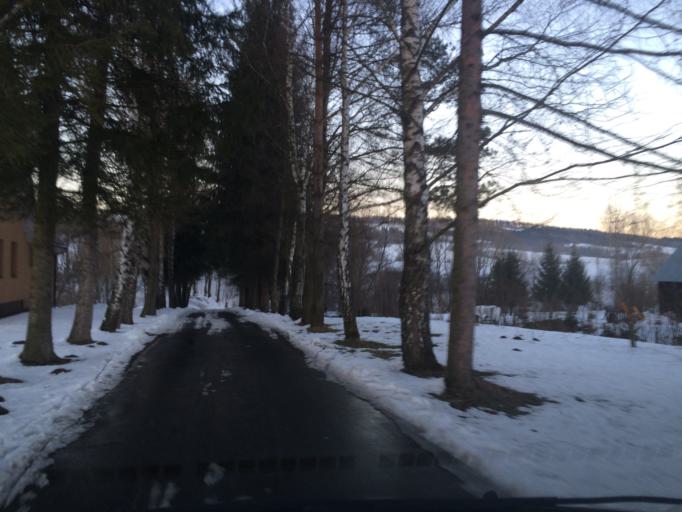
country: PL
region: Subcarpathian Voivodeship
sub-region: Powiat bieszczadzki
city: Ustrzyki Dolne
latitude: 49.4054
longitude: 22.5897
